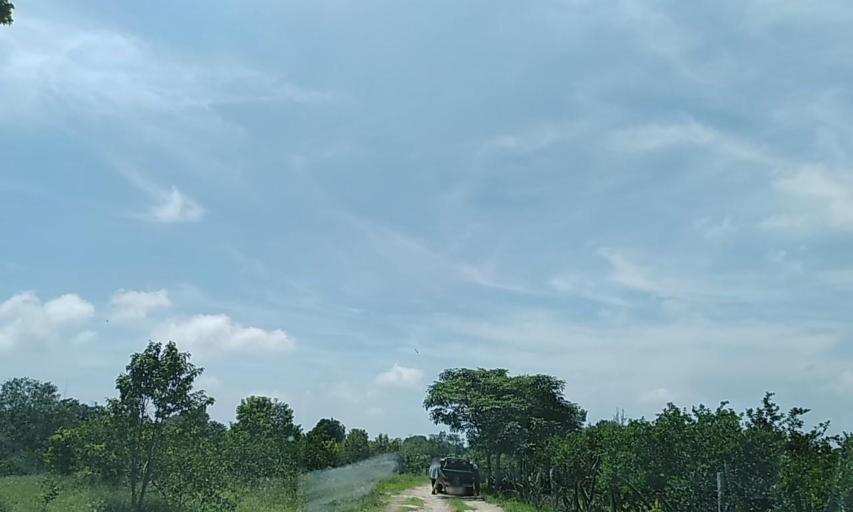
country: MX
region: Veracruz
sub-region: Emiliano Zapata
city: Dos Rios
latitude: 19.4424
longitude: -96.7607
